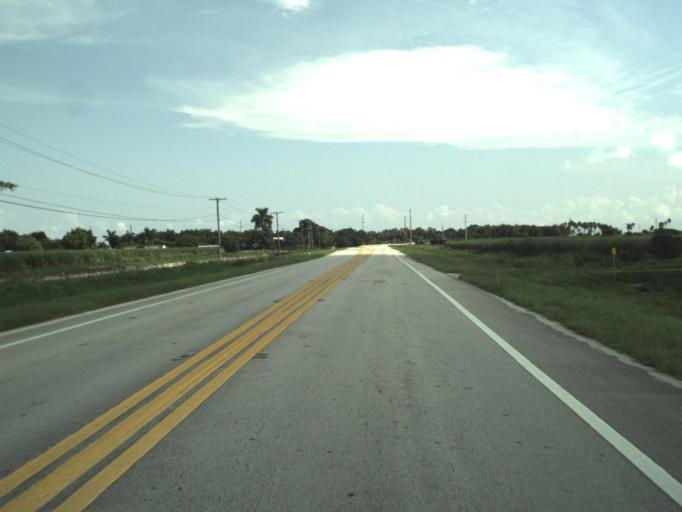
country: US
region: Florida
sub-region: Palm Beach County
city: Belle Glade
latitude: 26.7374
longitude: -80.6841
